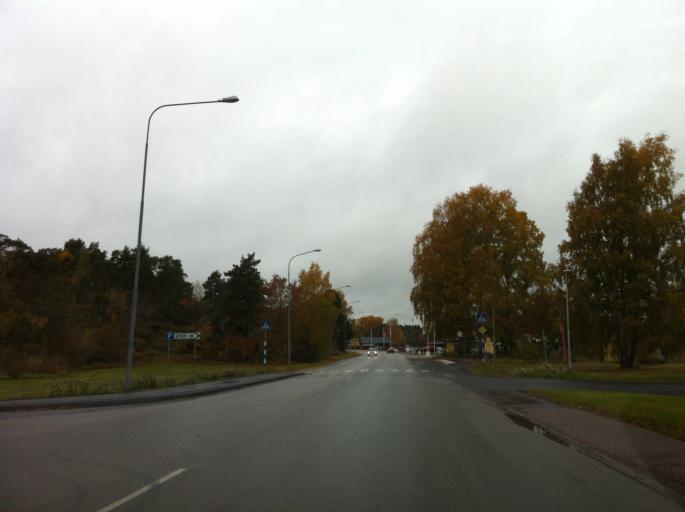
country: SE
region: Uppsala
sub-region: Osthammars Kommun
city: OEsthammar
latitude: 60.2593
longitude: 18.3655
